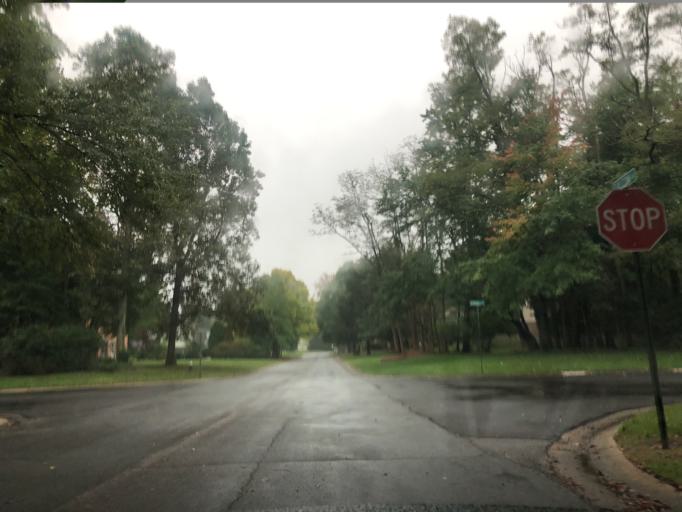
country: US
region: Ohio
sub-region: Hamilton County
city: The Village of Indian Hill
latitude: 39.2674
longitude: -84.2911
